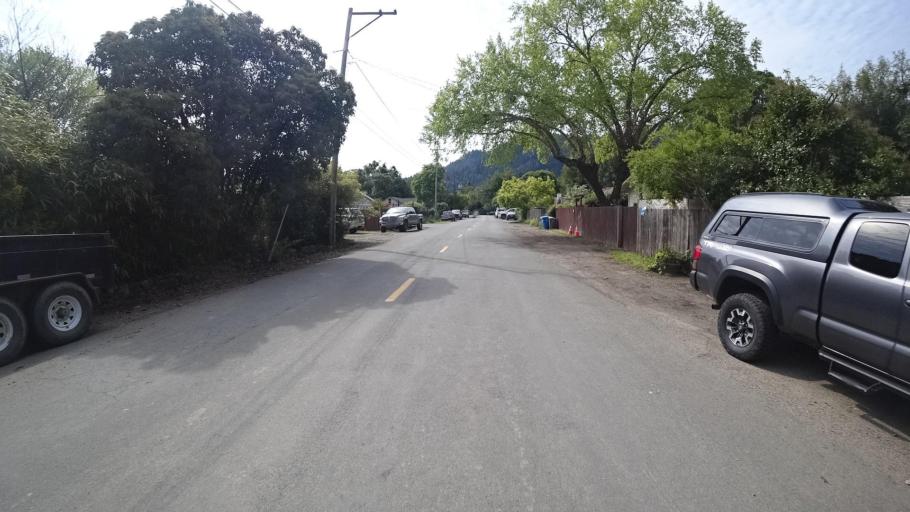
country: US
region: California
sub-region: Humboldt County
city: Redway
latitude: 40.1180
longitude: -123.8263
